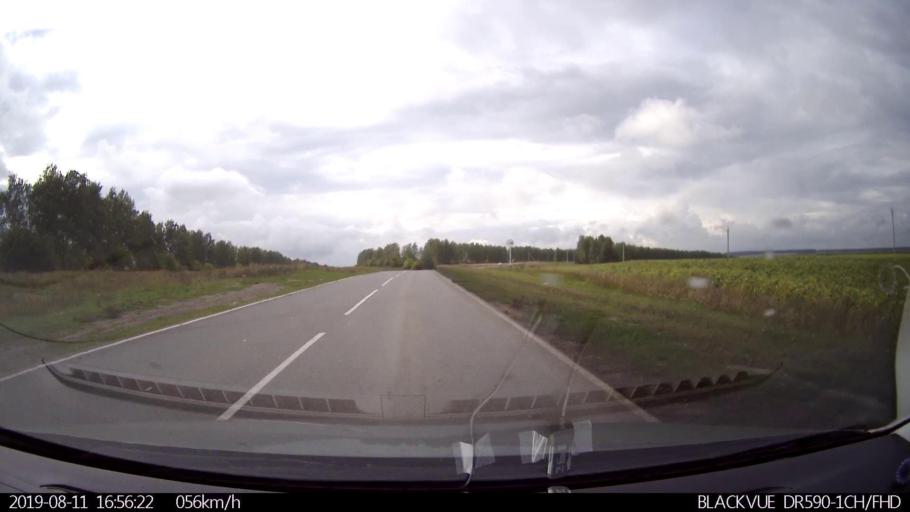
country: RU
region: Ulyanovsk
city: Mayna
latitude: 54.2871
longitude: 47.6544
